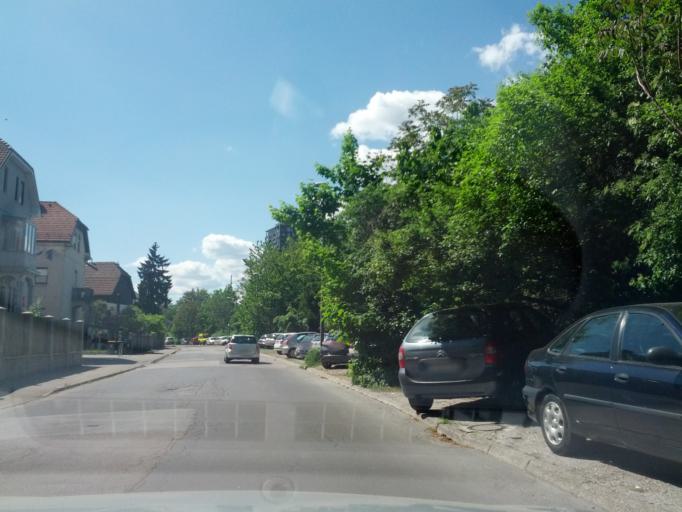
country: SI
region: Ljubljana
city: Ljubljana
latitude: 46.0580
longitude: 14.5256
